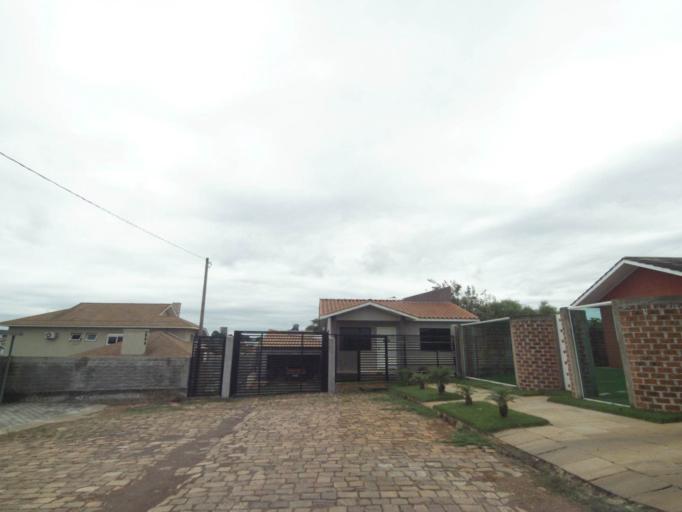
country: BR
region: Rio Grande do Sul
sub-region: Lagoa Vermelha
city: Lagoa Vermelha
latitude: -28.2163
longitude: -51.5343
